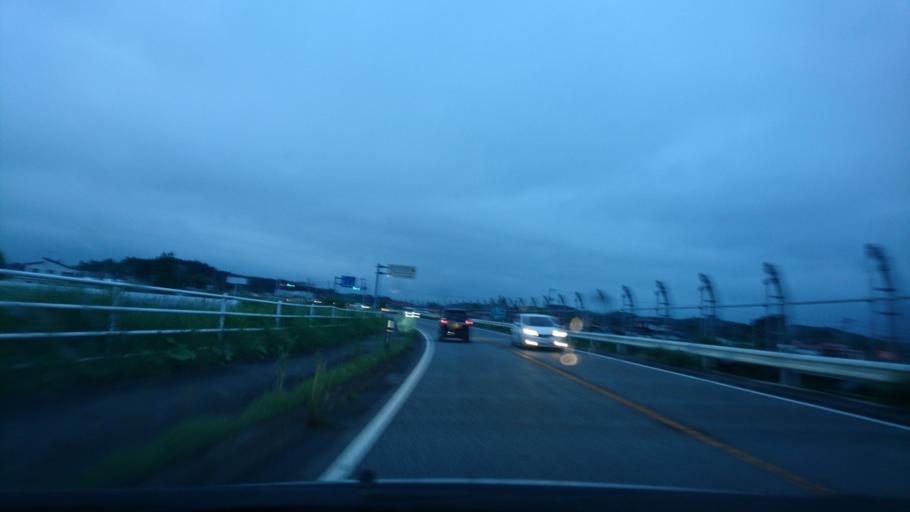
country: JP
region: Iwate
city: Ichinoseki
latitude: 38.8007
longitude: 141.0572
